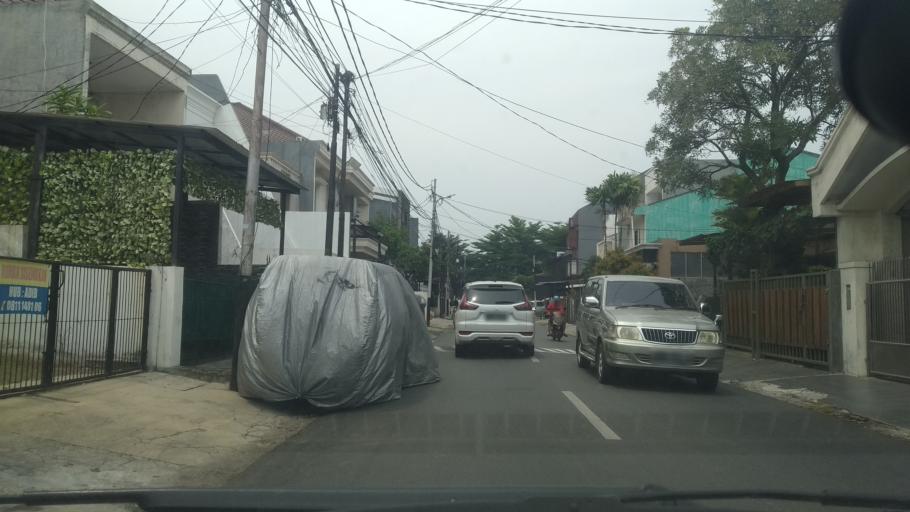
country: ID
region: Banten
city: South Tangerang
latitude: -6.2644
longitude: 106.7794
